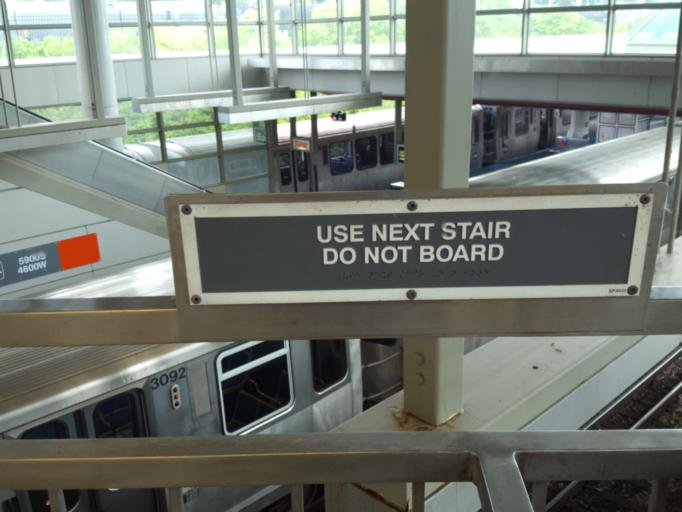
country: US
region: Illinois
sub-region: Cook County
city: Hometown
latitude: 41.7866
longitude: -87.7381
